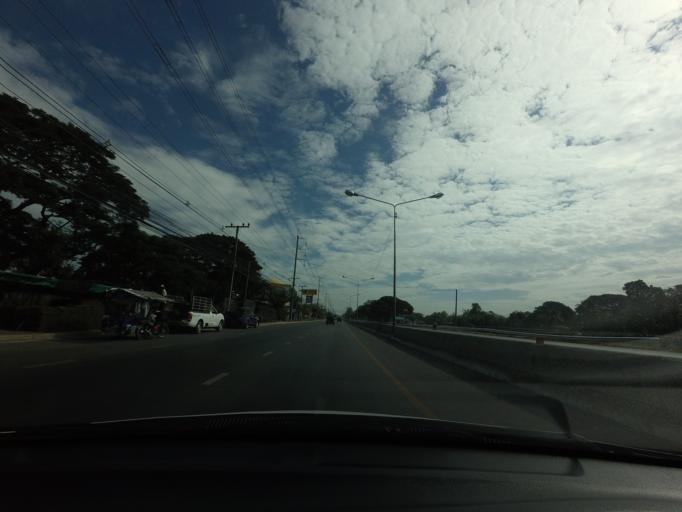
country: TH
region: Pathum Thani
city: Ban Rangsit
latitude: 14.0504
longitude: 100.8172
